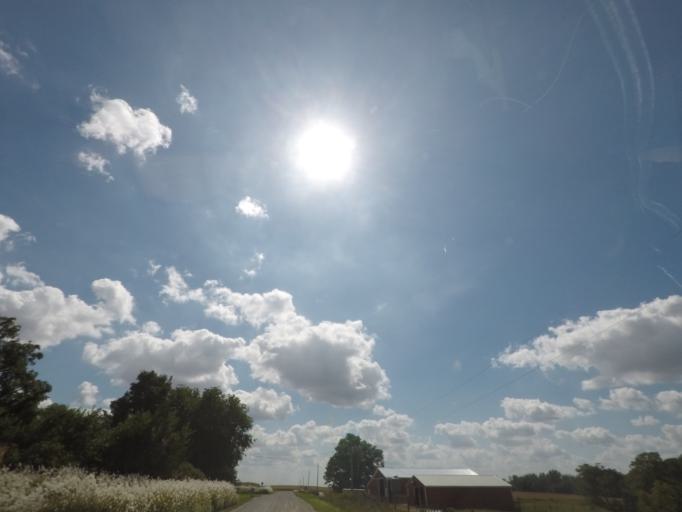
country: US
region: Iowa
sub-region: Story County
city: Nevada
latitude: 42.0450
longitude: -93.3595
